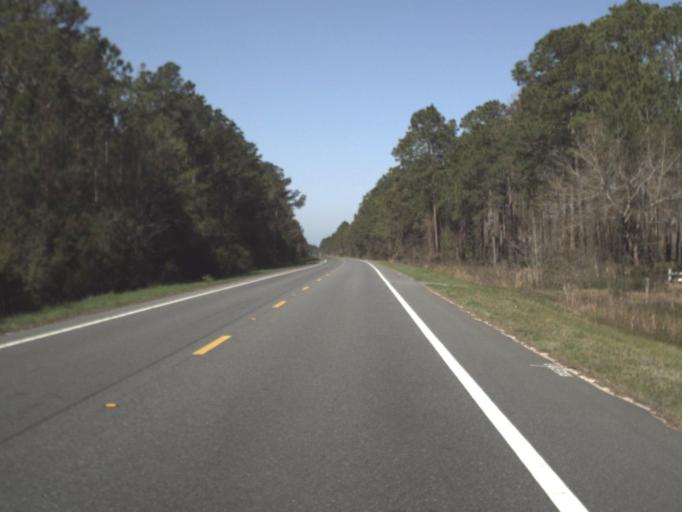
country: US
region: Florida
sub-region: Leon County
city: Woodville
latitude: 30.1904
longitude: -84.0595
